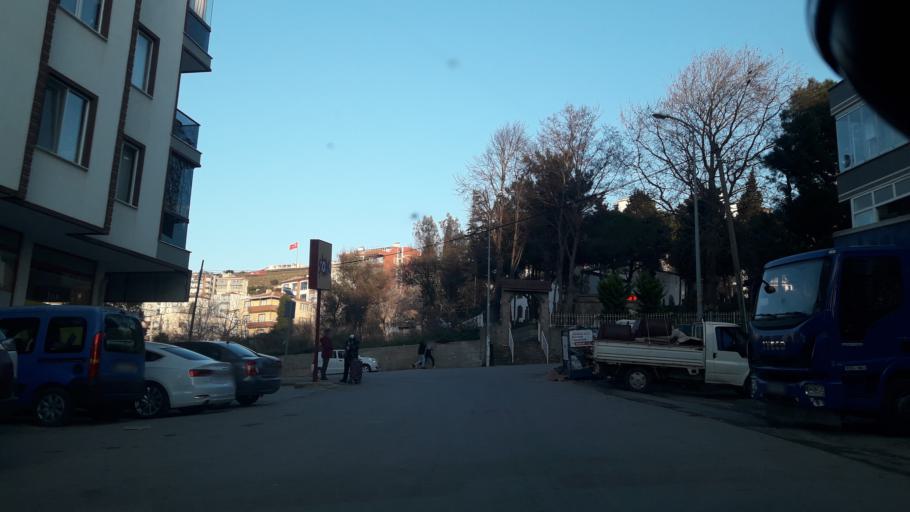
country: TR
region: Sinop
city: Sinop
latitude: 42.0251
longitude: 35.1610
